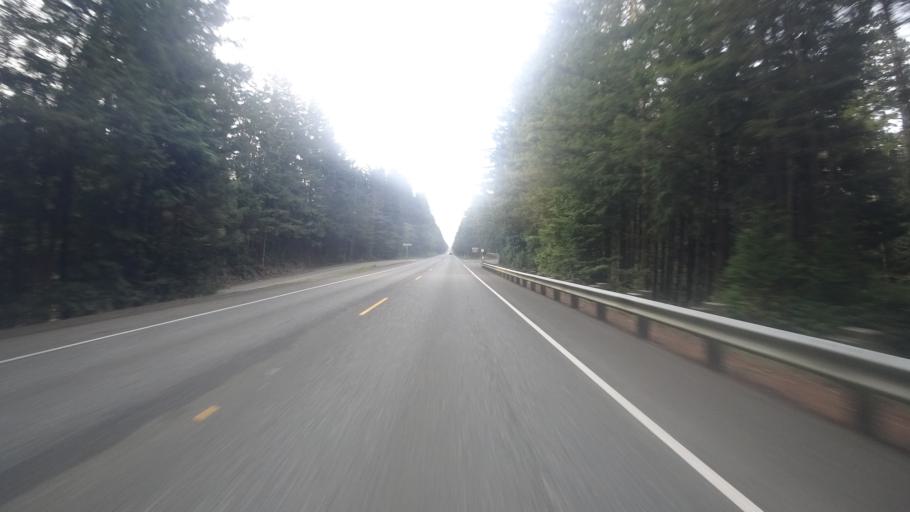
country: US
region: Oregon
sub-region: Coos County
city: Lakeside
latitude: 43.5347
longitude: -124.2154
